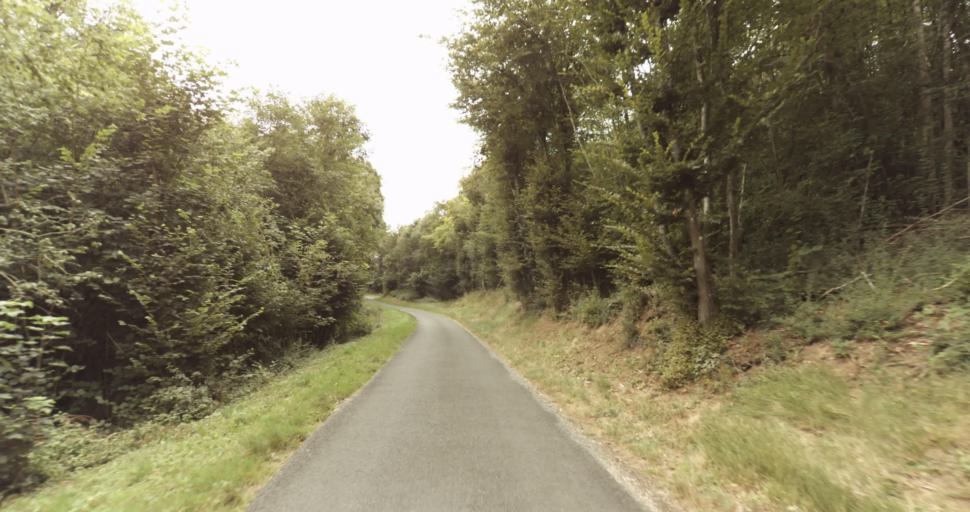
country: FR
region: Haute-Normandie
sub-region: Departement de l'Eure
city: Menilles
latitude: 49.0293
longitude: 1.3133
